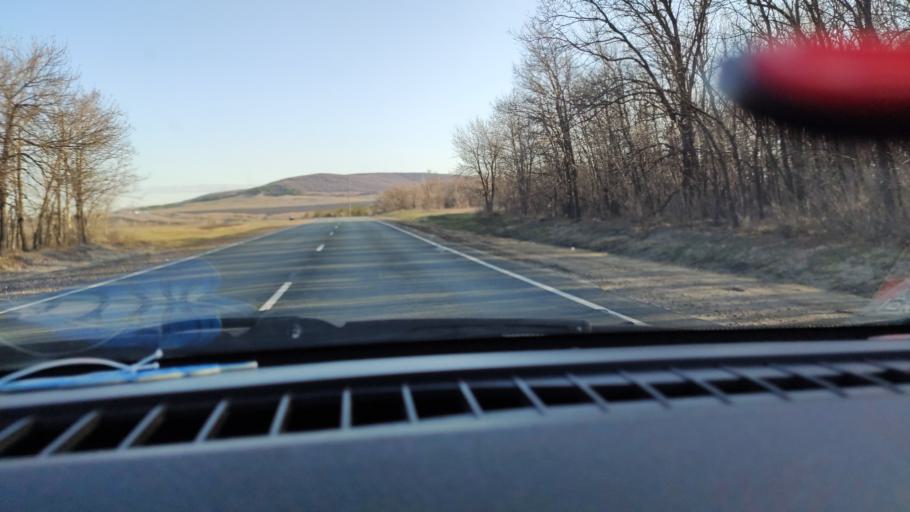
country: RU
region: Saratov
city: Alekseyevka
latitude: 52.2753
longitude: 47.9309
